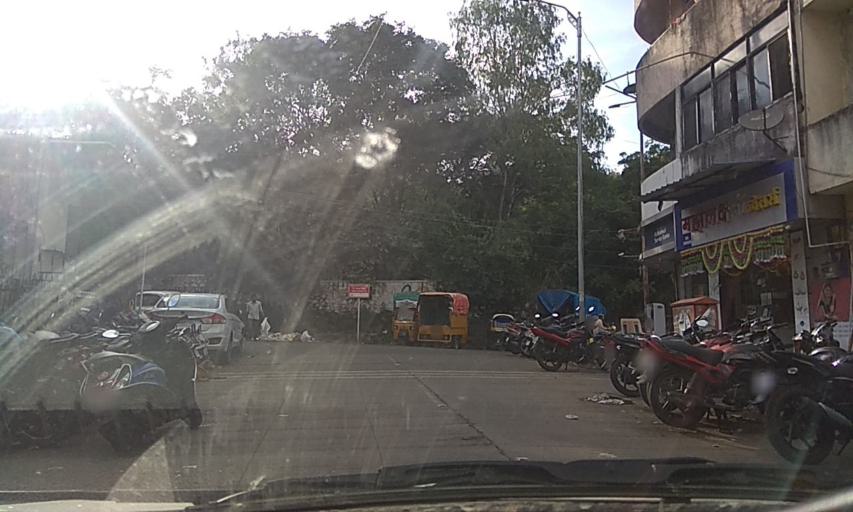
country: IN
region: Maharashtra
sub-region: Pune Division
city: Pune
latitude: 18.4975
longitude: 73.8498
